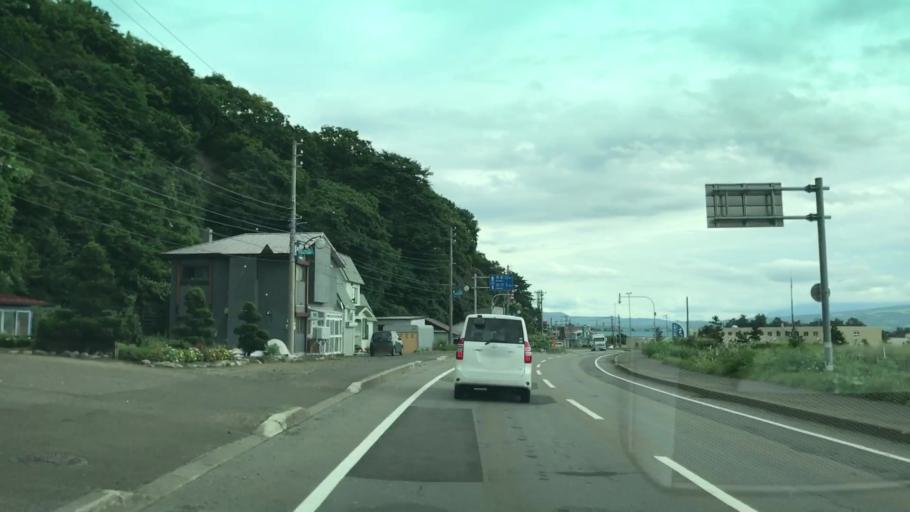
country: JP
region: Hokkaido
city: Iwanai
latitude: 43.0340
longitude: 140.5302
